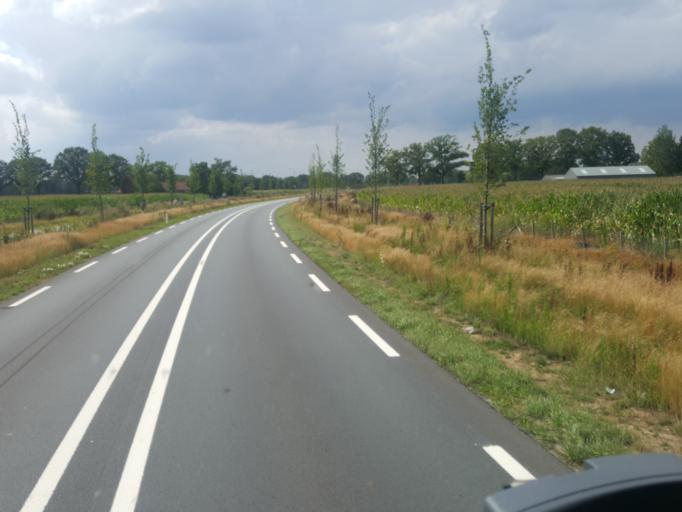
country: NL
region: North Brabant
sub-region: Gemeente Cuijk
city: Cuijk
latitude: 51.6799
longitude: 5.8534
